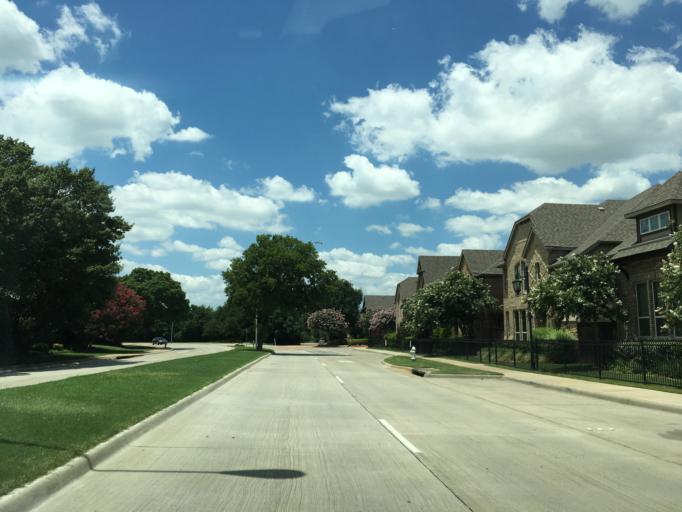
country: US
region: Texas
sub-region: Dallas County
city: Addison
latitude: 32.9327
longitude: -96.8424
